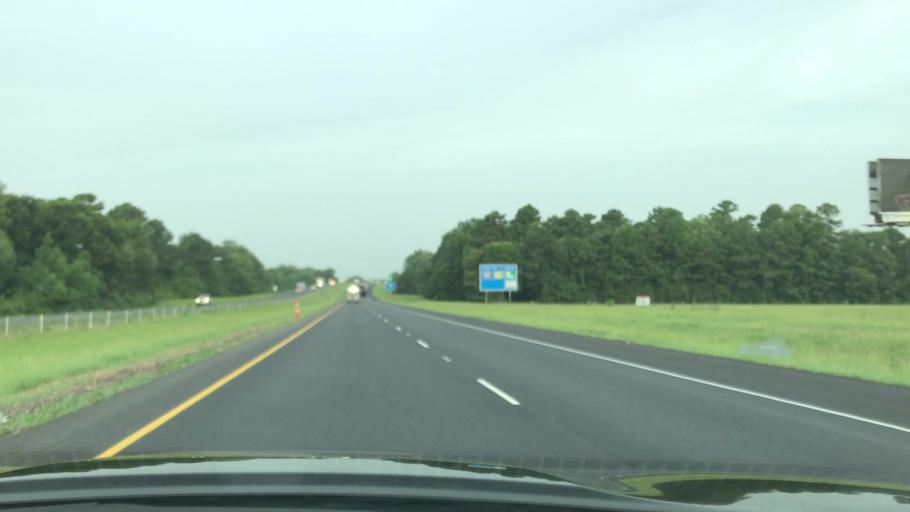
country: US
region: Louisiana
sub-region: Caddo Parish
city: Greenwood
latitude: 32.4445
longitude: -93.9296
